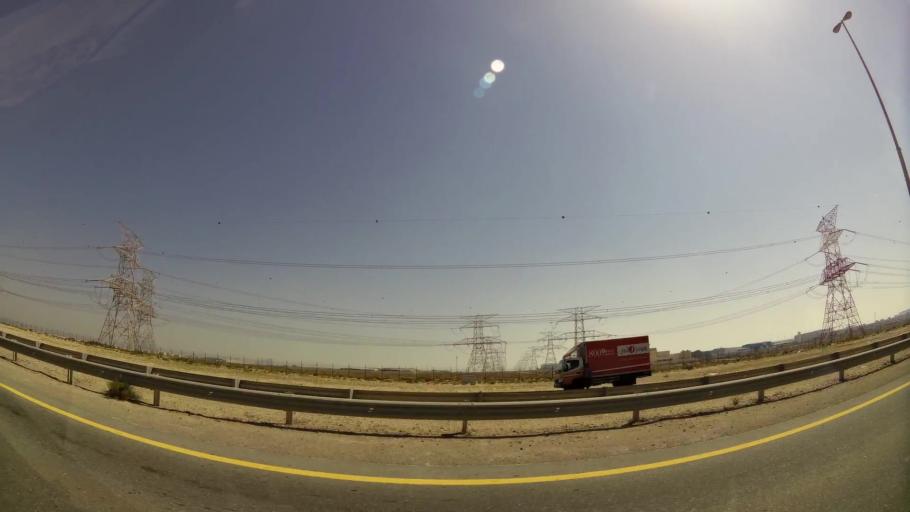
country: AE
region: Dubai
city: Dubai
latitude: 24.9325
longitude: 55.0833
